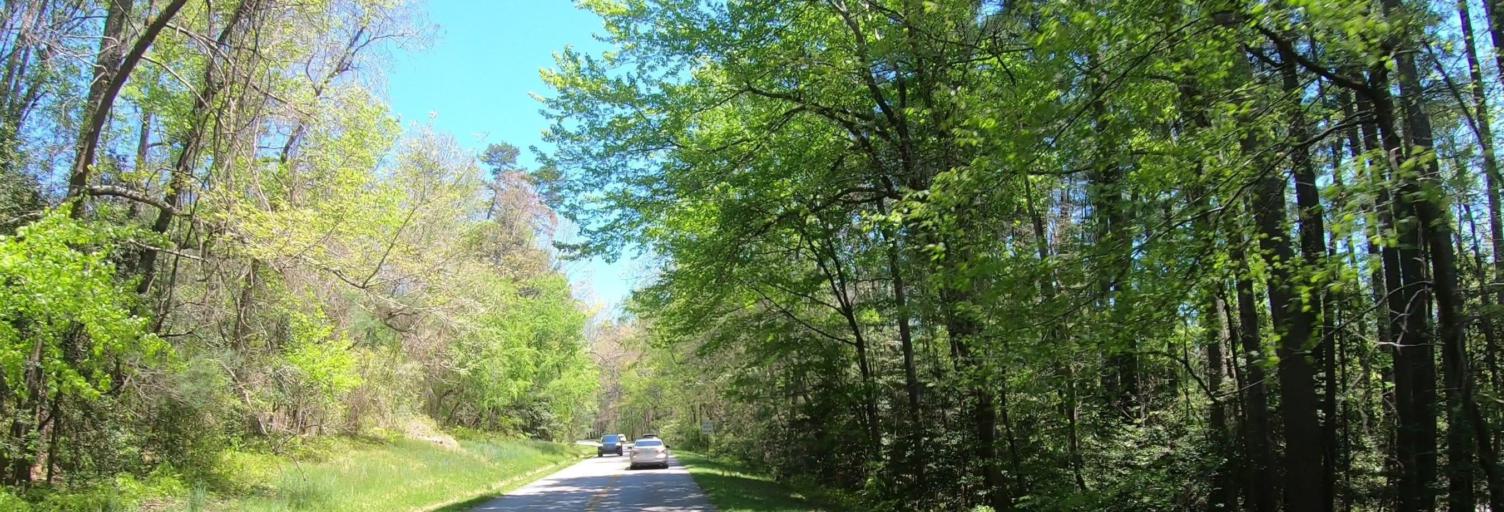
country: US
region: North Carolina
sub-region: Buncombe County
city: Biltmore Forest
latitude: 35.5176
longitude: -82.5349
